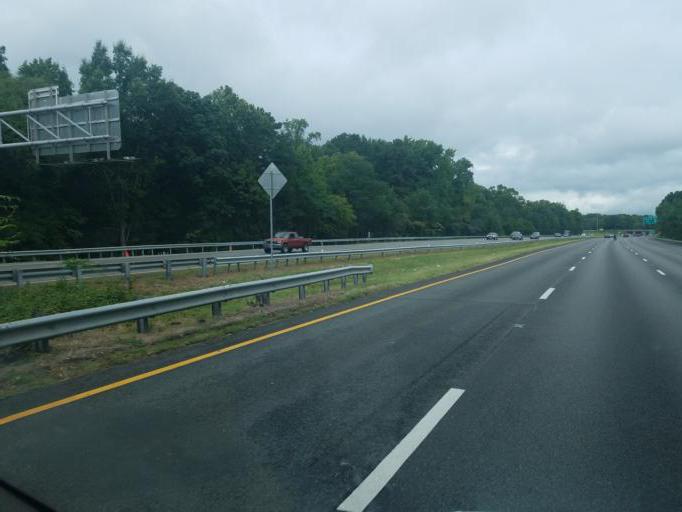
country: US
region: Virginia
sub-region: Henrico County
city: Chamberlayne
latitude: 37.6298
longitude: -77.4490
